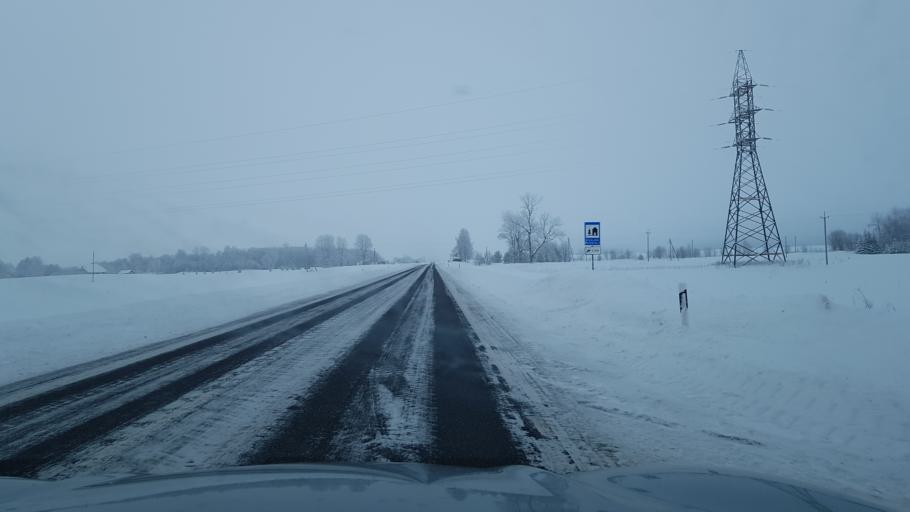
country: EE
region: Ida-Virumaa
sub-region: Johvi vald
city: Johvi
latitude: 59.2392
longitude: 27.3546
